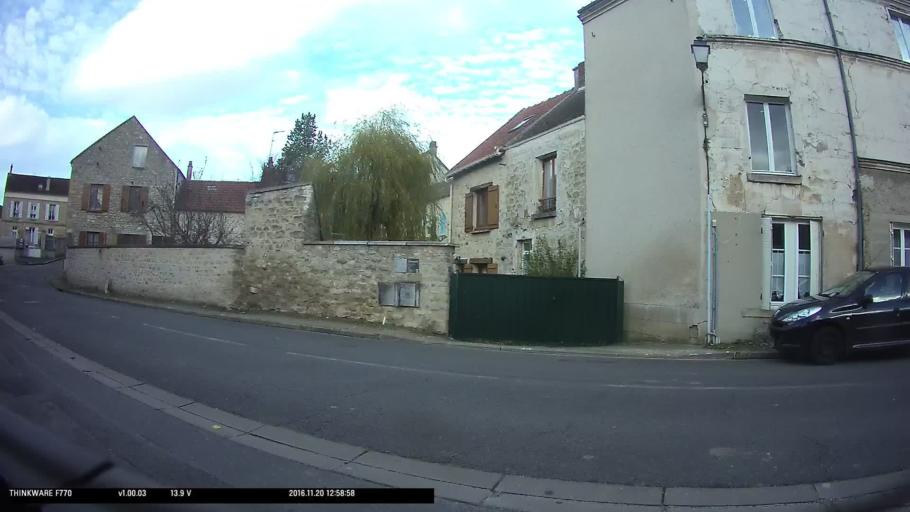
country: FR
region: Ile-de-France
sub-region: Departement du Val-d'Oise
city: Sagy
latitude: 49.0500
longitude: 1.9512
